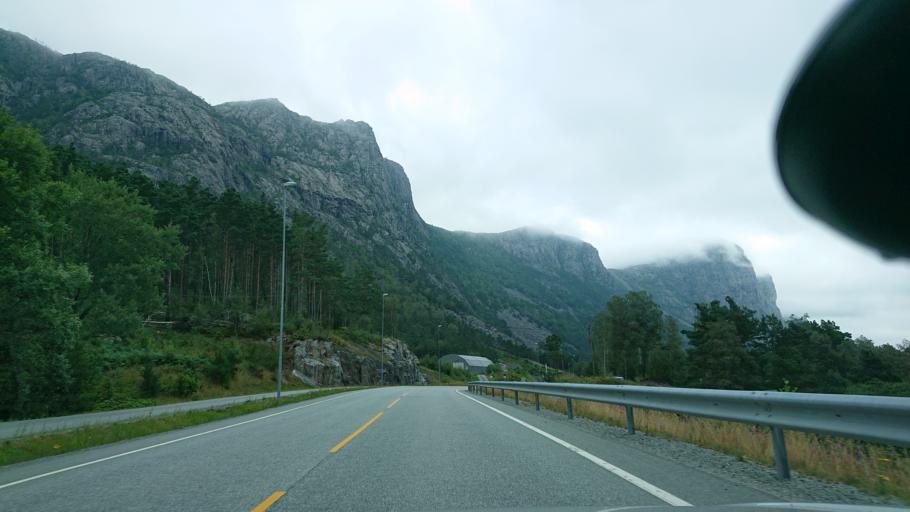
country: NO
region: Rogaland
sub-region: Strand
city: Jorpeland
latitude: 59.0760
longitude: 6.0653
